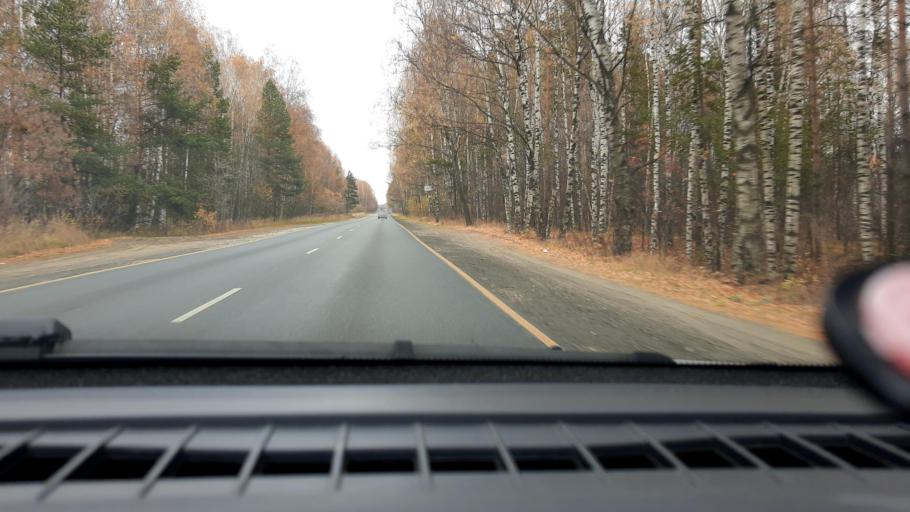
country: RU
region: Nizjnij Novgorod
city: Gorbatovka
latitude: 56.2613
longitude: 43.6862
